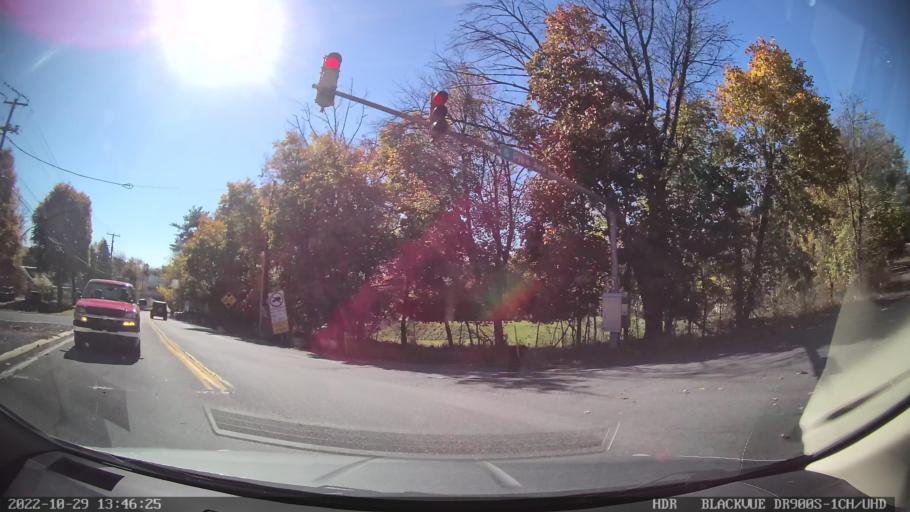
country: US
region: Pennsylvania
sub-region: Lehigh County
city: Fountain Hill
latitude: 40.5594
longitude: -75.4385
